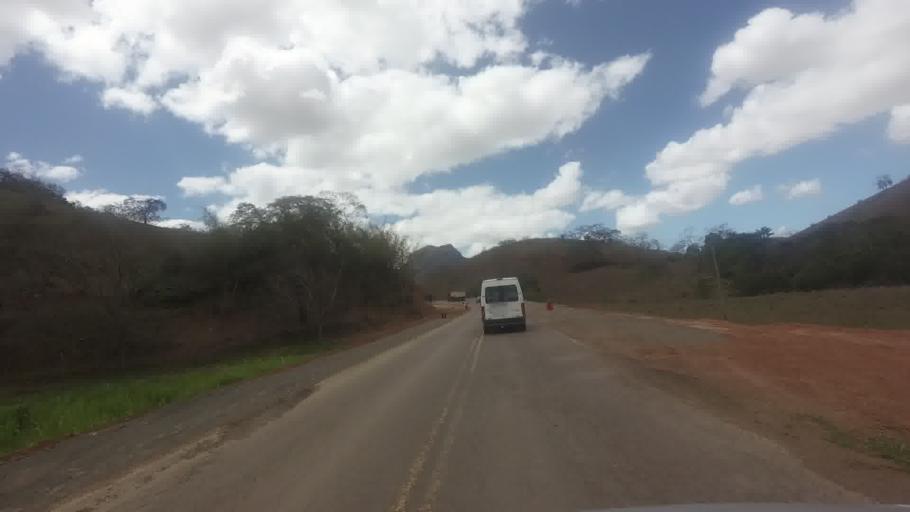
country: BR
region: Rio de Janeiro
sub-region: Santo Antonio De Padua
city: Santo Antonio de Padua
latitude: -21.5155
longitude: -42.0992
